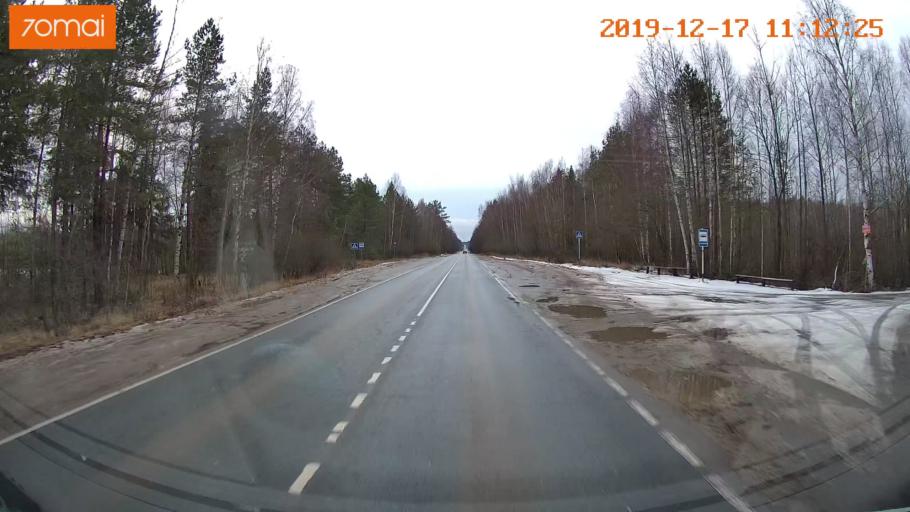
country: RU
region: Vladimir
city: Gus'-Khrustal'nyy
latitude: 55.5761
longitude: 40.6286
